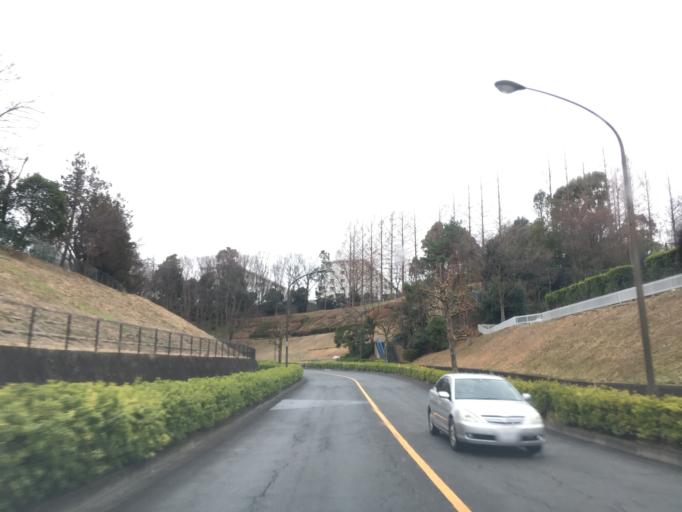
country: JP
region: Tokyo
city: Hino
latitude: 35.6292
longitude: 139.4134
